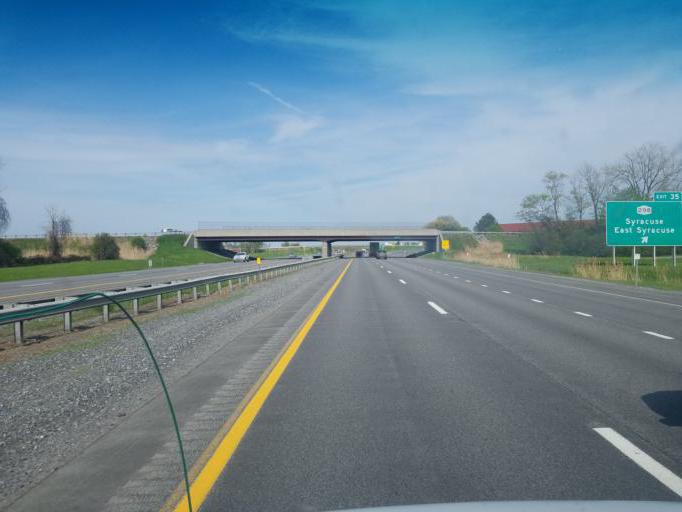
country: US
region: New York
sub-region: Onondaga County
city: East Syracuse
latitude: 43.0921
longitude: -76.0954
